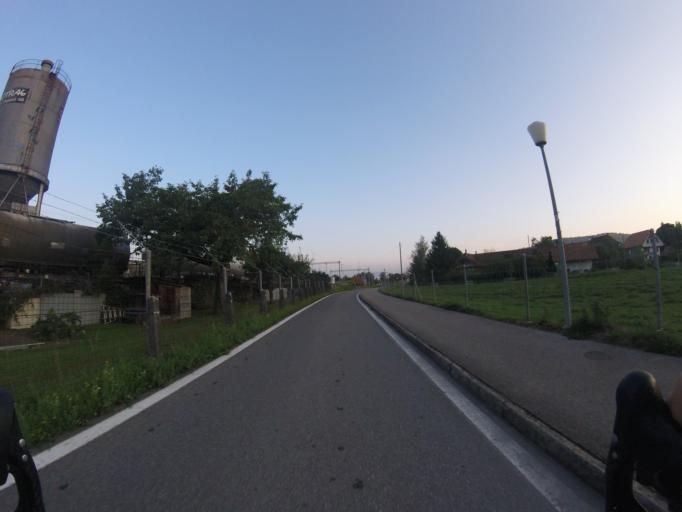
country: CH
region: Bern
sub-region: Thun District
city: Steffisburg
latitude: 46.7706
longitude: 7.6165
